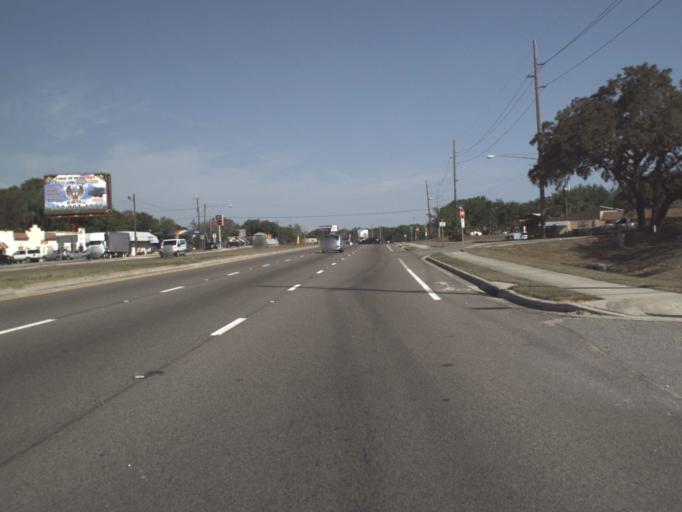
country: US
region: Florida
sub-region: Lake County
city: Minneola
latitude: 28.5768
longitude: -81.7488
